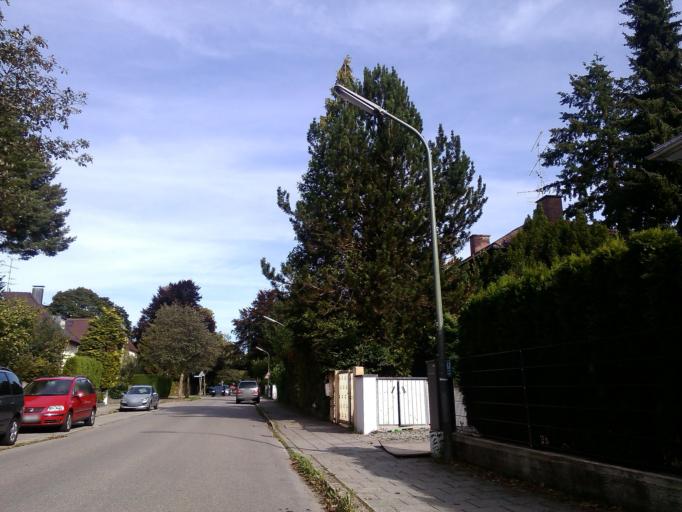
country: DE
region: Bavaria
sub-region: Upper Bavaria
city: Pullach im Isartal
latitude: 48.0725
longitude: 11.5158
